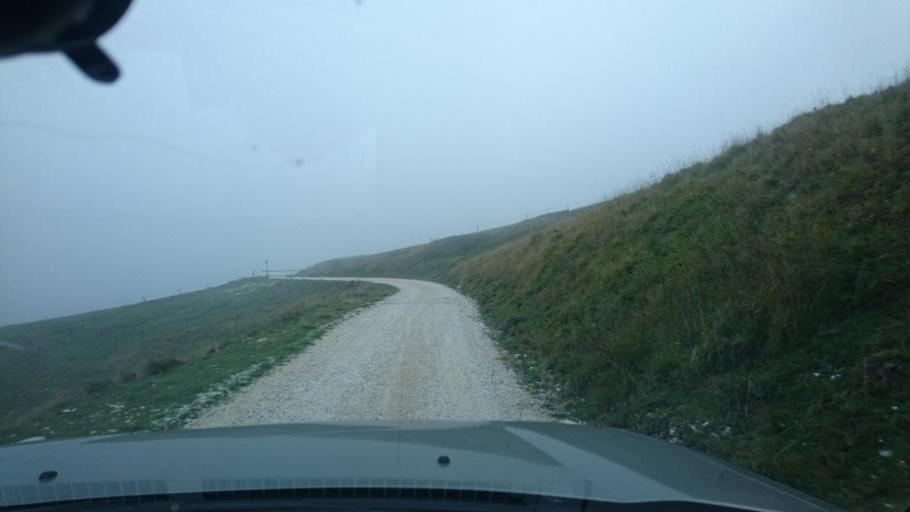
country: IT
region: Veneto
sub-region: Provincia di Vicenza
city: Enego
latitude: 45.9420
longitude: 11.6636
